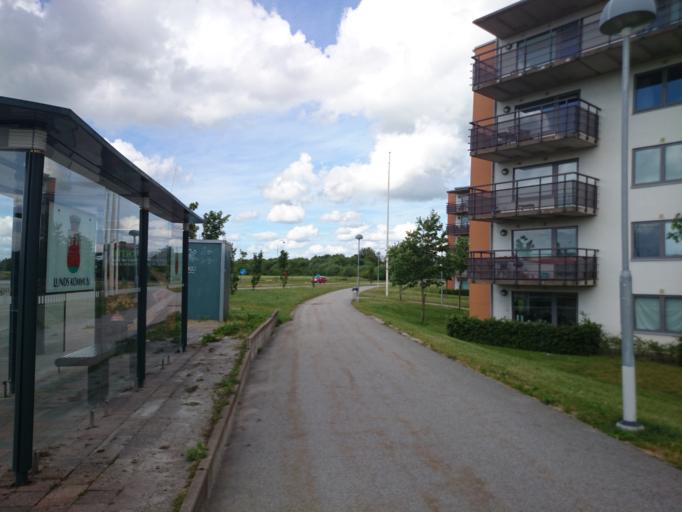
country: SE
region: Skane
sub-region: Lunds Kommun
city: Lund
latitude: 55.7184
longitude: 13.2349
